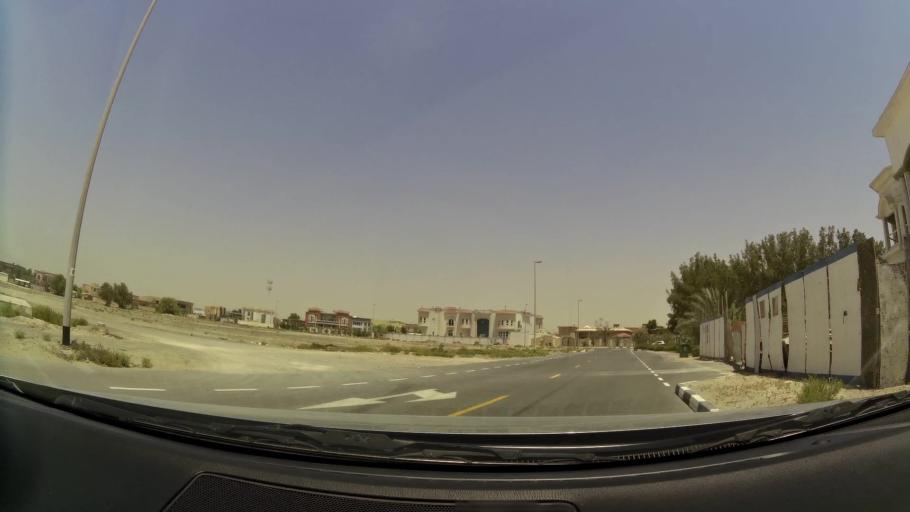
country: AE
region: Dubai
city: Dubai
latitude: 25.0857
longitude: 55.2049
